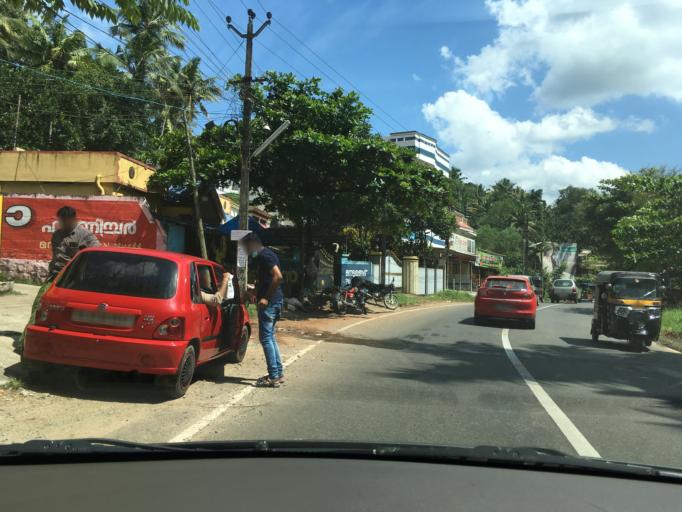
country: IN
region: Kerala
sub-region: Thiruvananthapuram
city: Nedumangad
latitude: 8.5800
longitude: 76.9956
